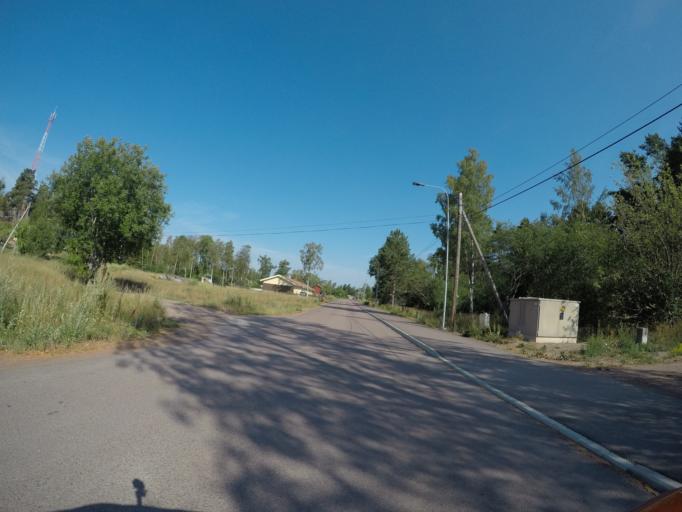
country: AX
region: Alands landsbygd
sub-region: Finstroem
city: Finstroem
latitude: 60.2253
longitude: 19.9804
